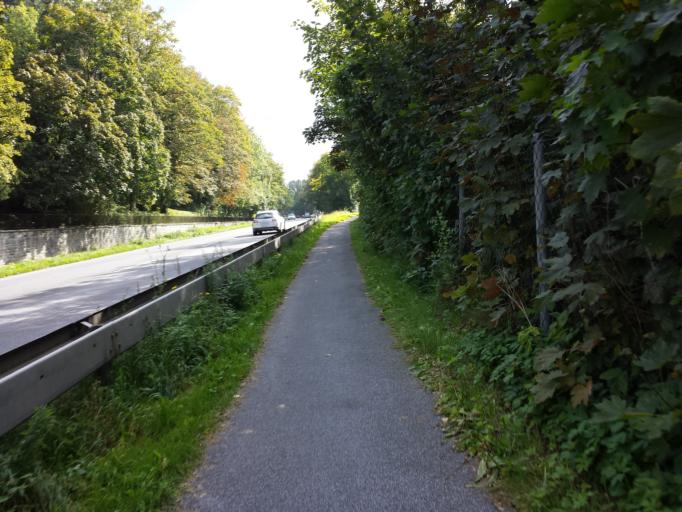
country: DE
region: North Rhine-Westphalia
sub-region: Regierungsbezirk Detmold
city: Langenberg
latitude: 51.7862
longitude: 8.3208
